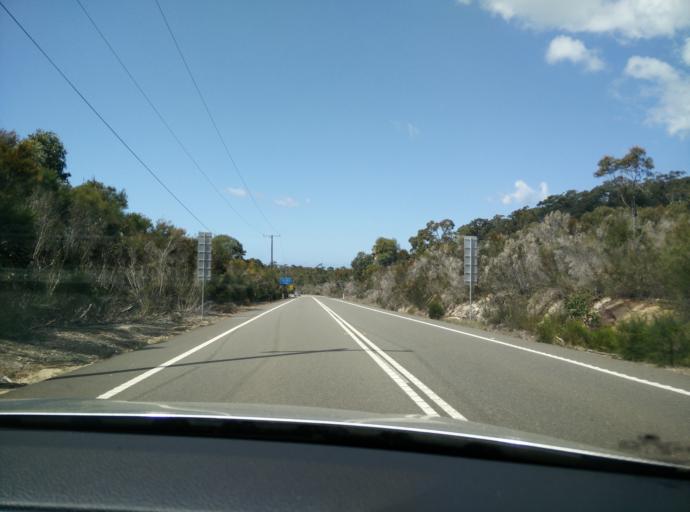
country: AU
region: New South Wales
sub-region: Gosford Shire
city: Blackwall
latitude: -33.4833
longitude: 151.2970
